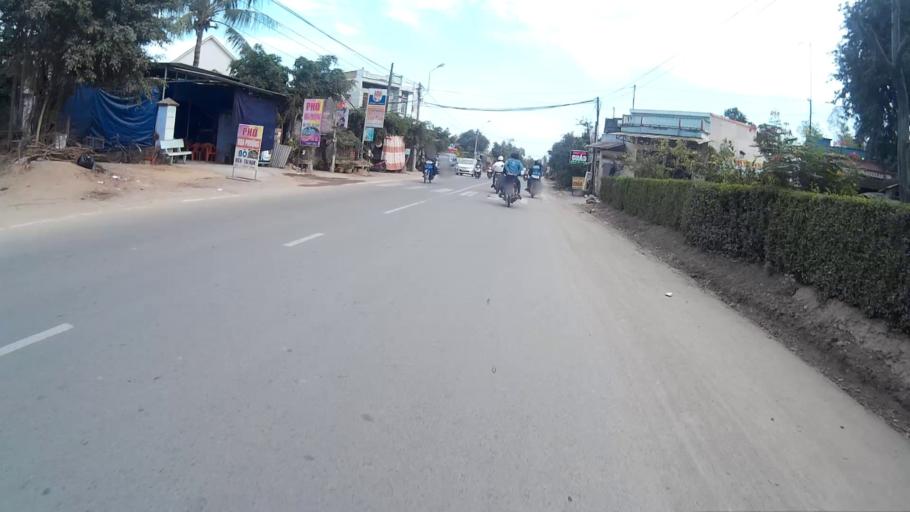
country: VN
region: Binh Dinh
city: An Nhon
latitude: 13.8628
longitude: 109.1330
